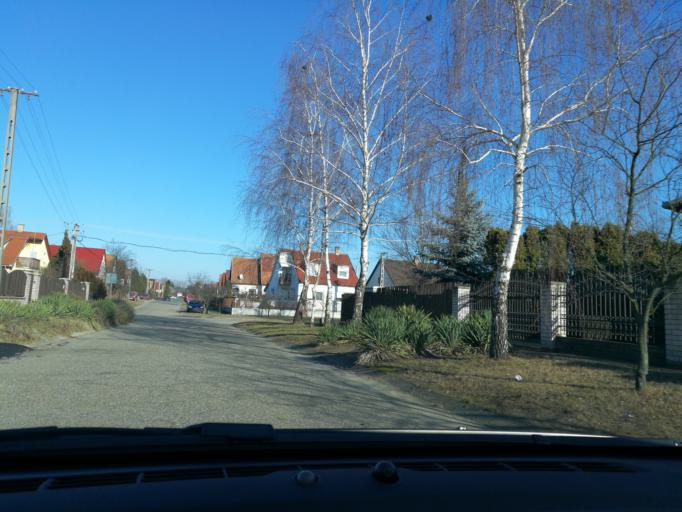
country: HU
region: Szabolcs-Szatmar-Bereg
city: Nyiregyhaza
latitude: 47.9245
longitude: 21.7555
